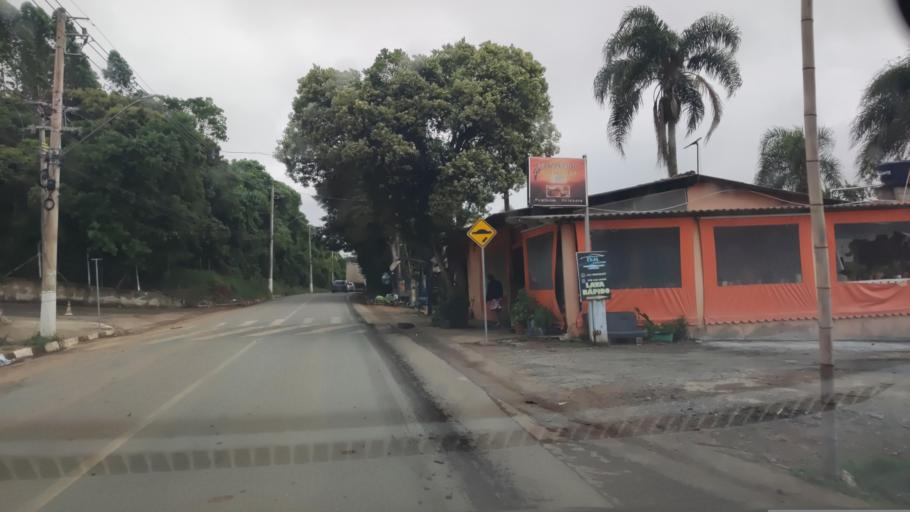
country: BR
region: Sao Paulo
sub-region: Vargem Grande Paulista
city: Vargem Grande Paulista
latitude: -23.6550
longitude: -47.0489
